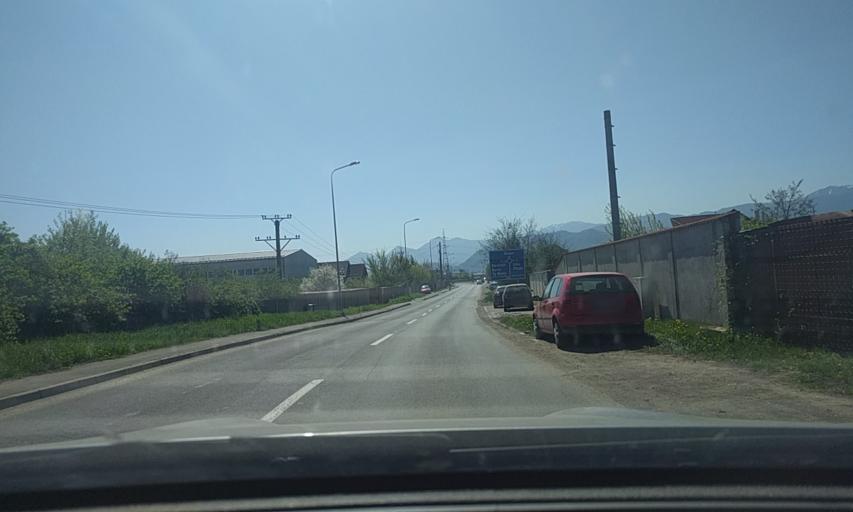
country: RO
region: Brasov
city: Brasov
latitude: 45.6902
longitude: 25.5665
